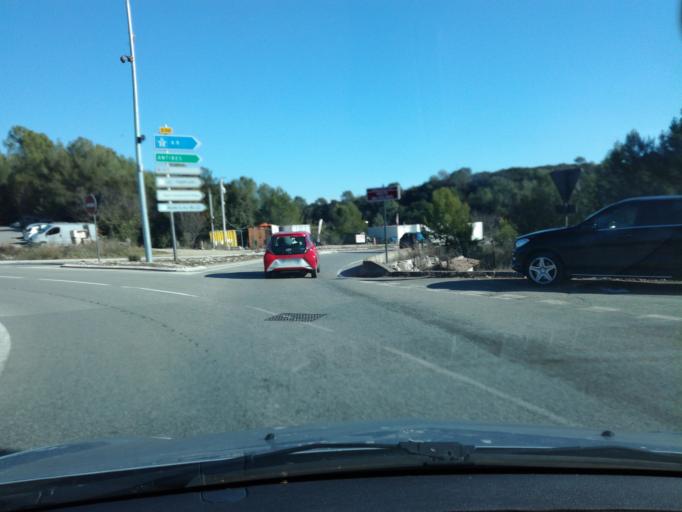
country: FR
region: Provence-Alpes-Cote d'Azur
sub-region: Departement des Alpes-Maritimes
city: Biot
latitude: 43.6203
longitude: 7.0639
